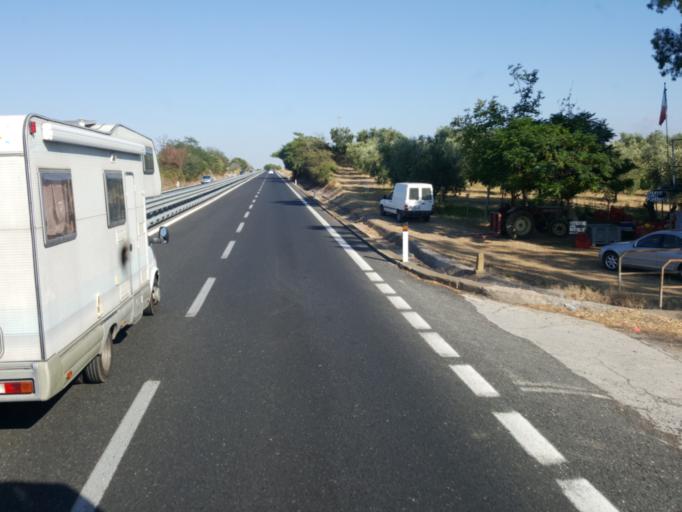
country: IT
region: Latium
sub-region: Provincia di Viterbo
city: Pescia Romana
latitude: 42.3932
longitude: 11.5314
